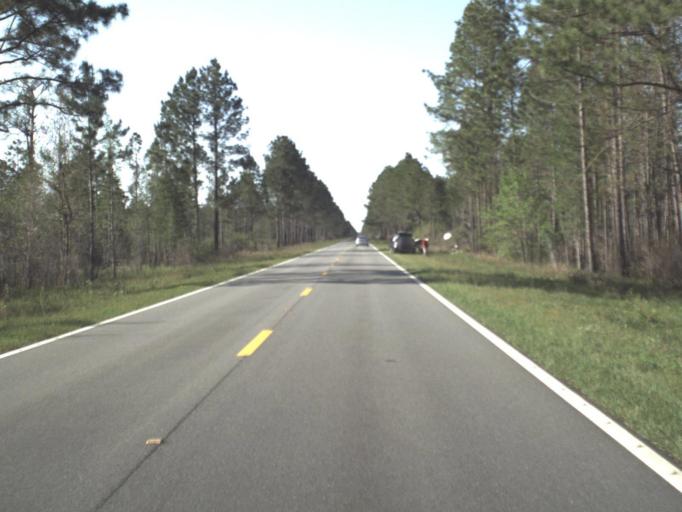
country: US
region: Florida
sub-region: Gulf County
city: Wewahitchka
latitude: 30.0396
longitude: -84.9835
